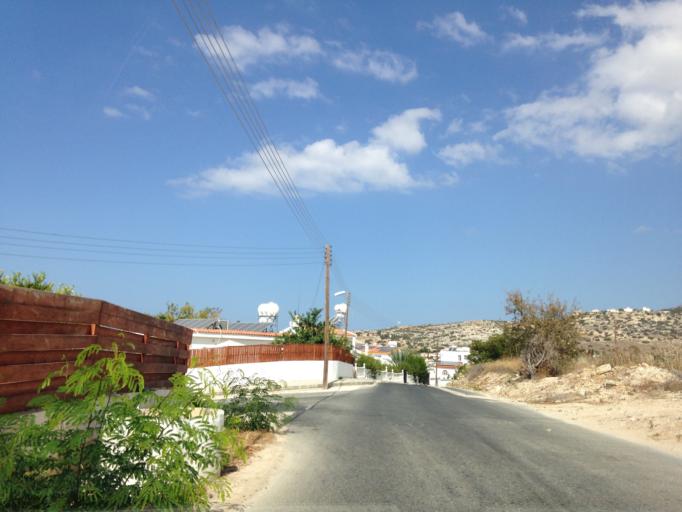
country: CY
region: Pafos
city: Pegeia
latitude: 34.8703
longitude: 32.3721
